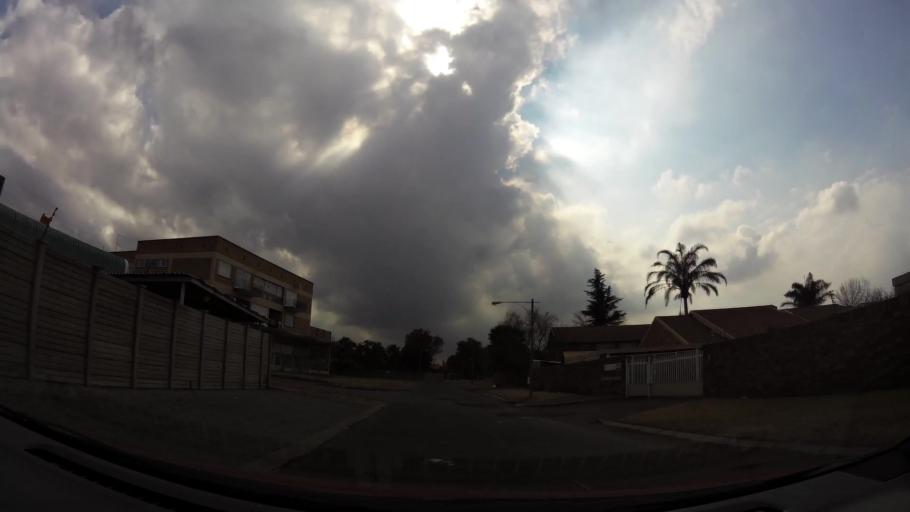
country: ZA
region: Gauteng
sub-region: Sedibeng District Municipality
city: Vanderbijlpark
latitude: -26.7123
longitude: 27.8418
